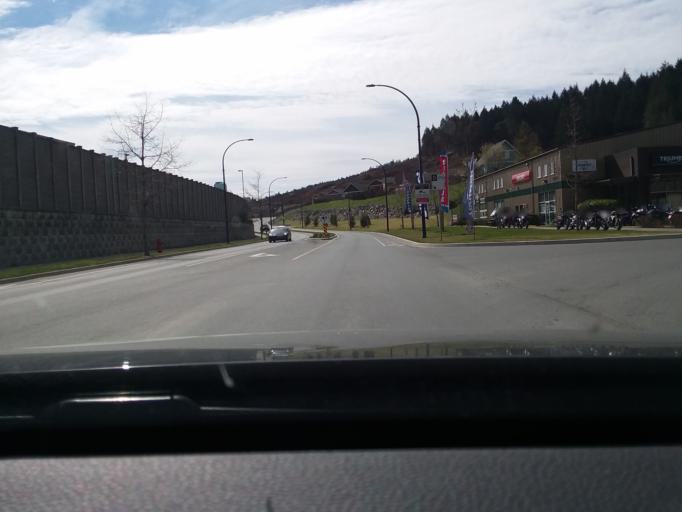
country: CA
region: British Columbia
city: Langford
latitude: 48.4532
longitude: -123.5416
